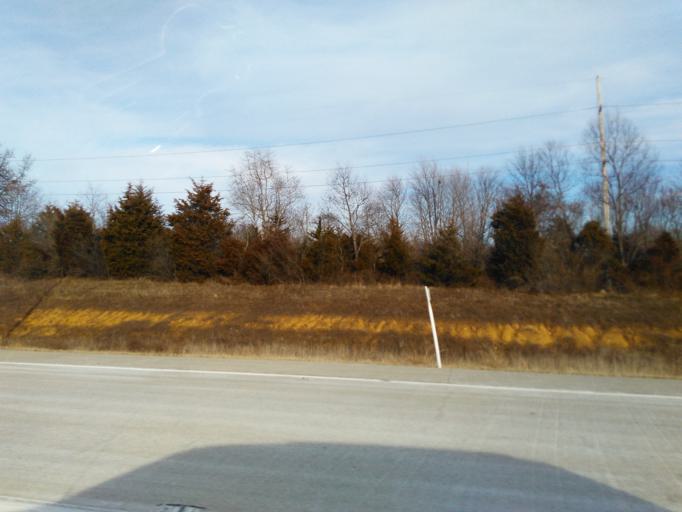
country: US
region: Illinois
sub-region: Jefferson County
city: Mount Vernon
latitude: 38.2950
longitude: -88.9441
